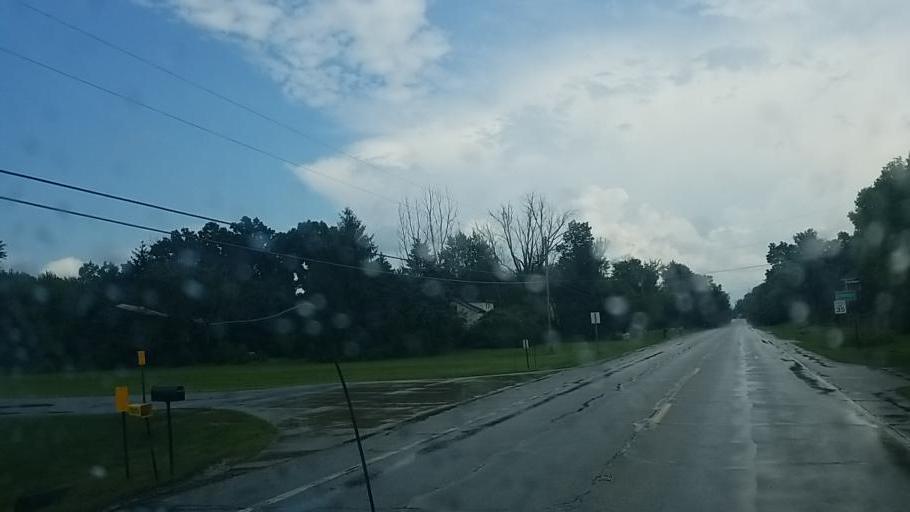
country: US
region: Ohio
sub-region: Lorain County
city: Grafton
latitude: 41.1680
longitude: -82.0311
